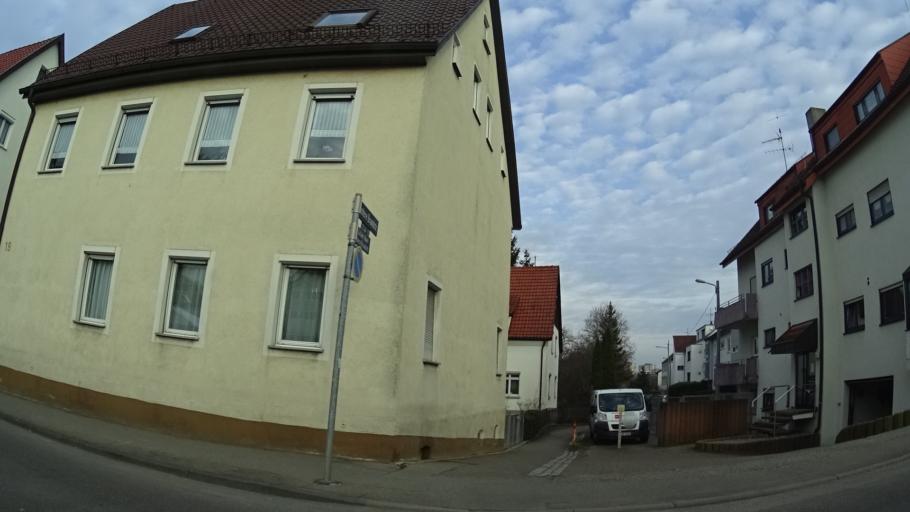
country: DE
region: Baden-Wuerttemberg
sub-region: Regierungsbezirk Stuttgart
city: Leinfelden-Echterdingen
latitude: 48.7246
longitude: 9.1466
